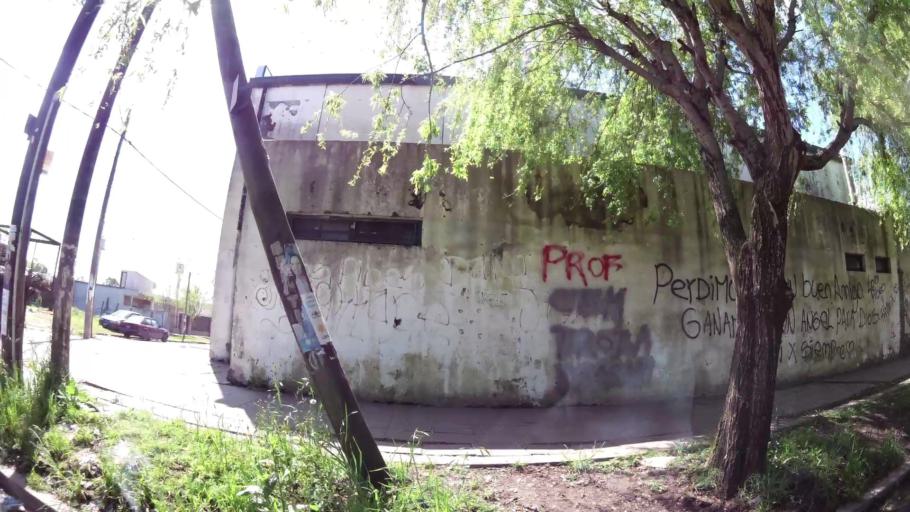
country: AR
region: Buenos Aires
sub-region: Partido de Quilmes
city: Quilmes
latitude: -34.8216
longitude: -58.2574
